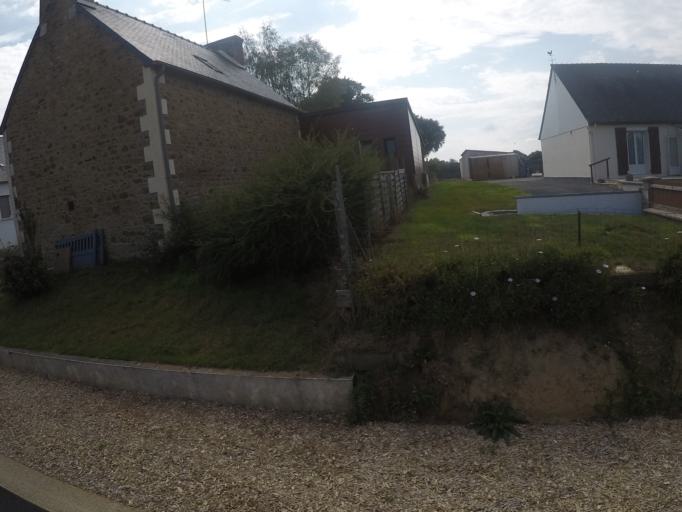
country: FR
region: Brittany
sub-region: Departement des Cotes-d'Armor
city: Goudelin
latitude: 48.6018
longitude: -3.0161
